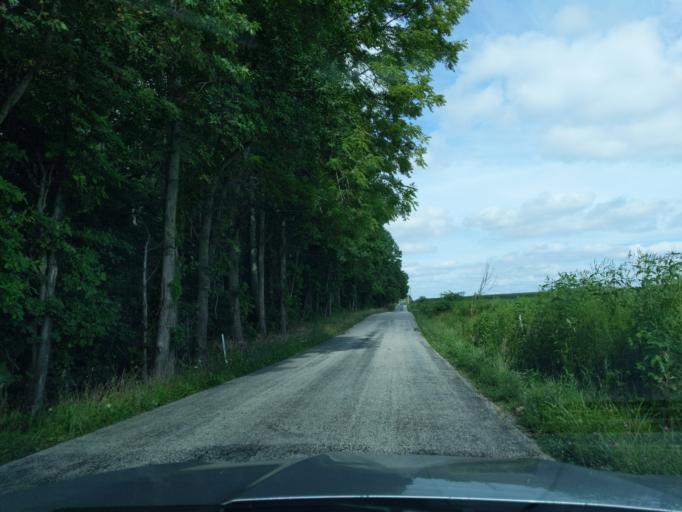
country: US
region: Indiana
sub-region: Decatur County
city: Greensburg
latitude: 39.2350
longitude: -85.3959
